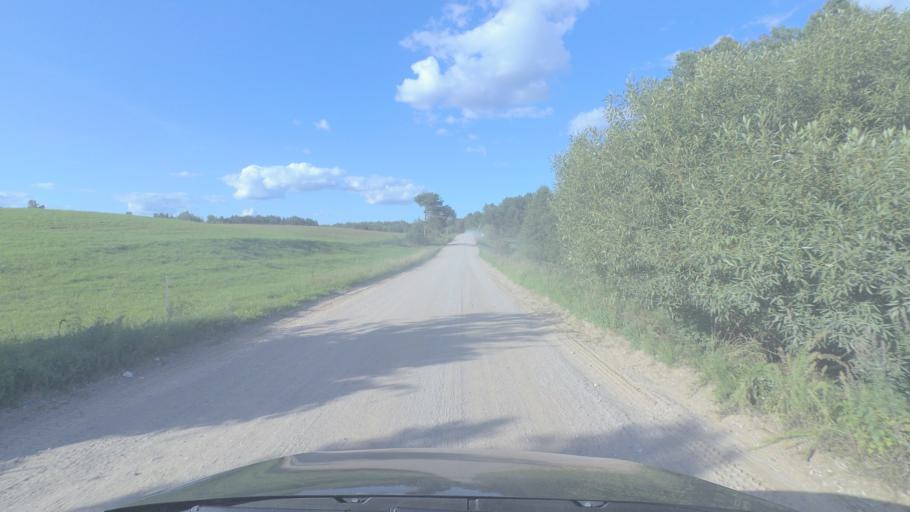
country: LT
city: Pabrade
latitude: 55.1380
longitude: 25.7105
